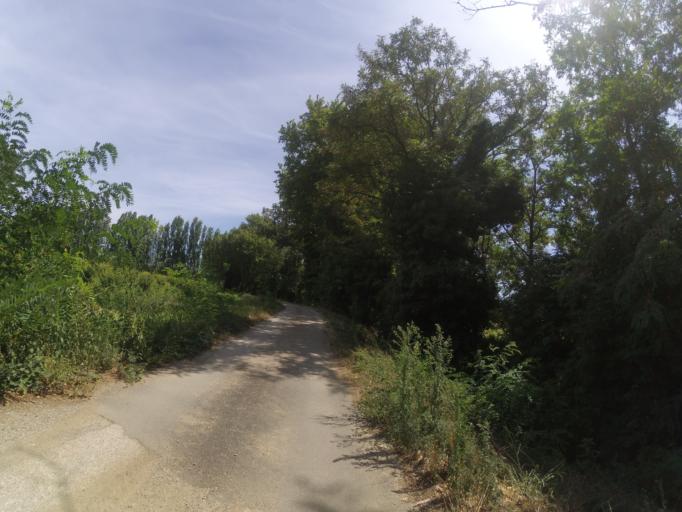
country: FR
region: Languedoc-Roussillon
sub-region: Departement des Pyrenees-Orientales
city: Ille-sur-Tet
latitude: 42.6767
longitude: 2.6488
